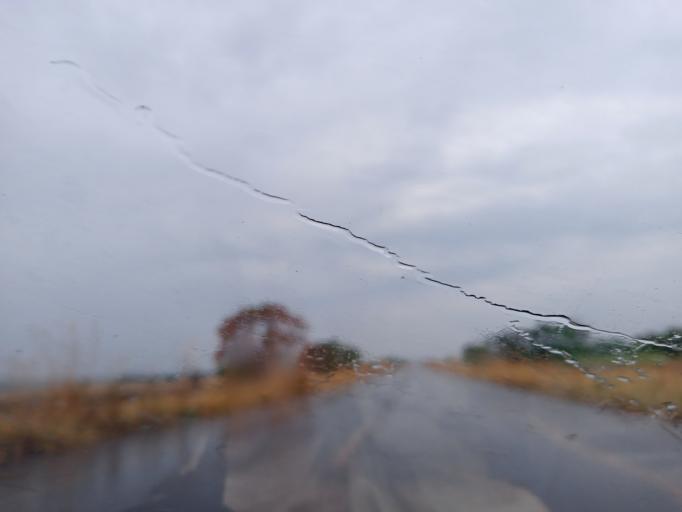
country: BR
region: Minas Gerais
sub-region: Ituiutaba
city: Ituiutaba
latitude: -19.0900
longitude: -49.5101
